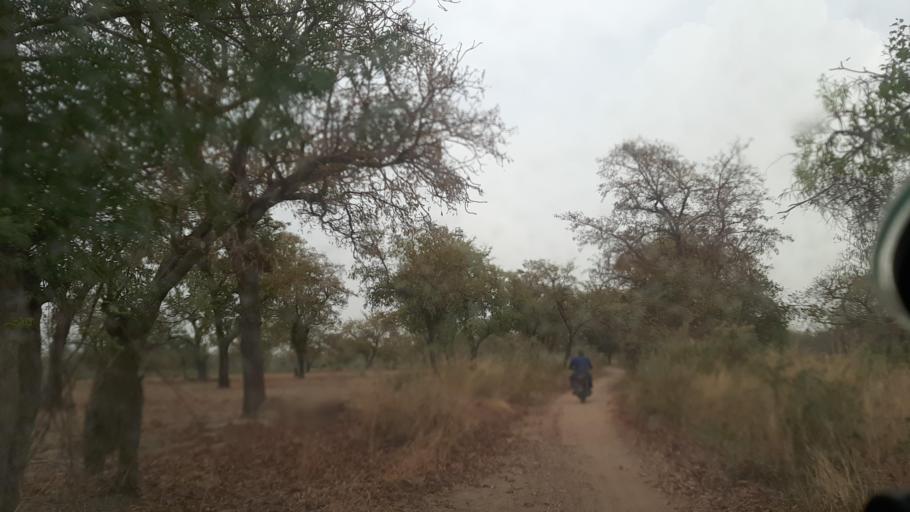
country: BF
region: Boucle du Mouhoun
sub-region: Province des Banwa
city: Salanso
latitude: 11.8565
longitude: -4.4309
